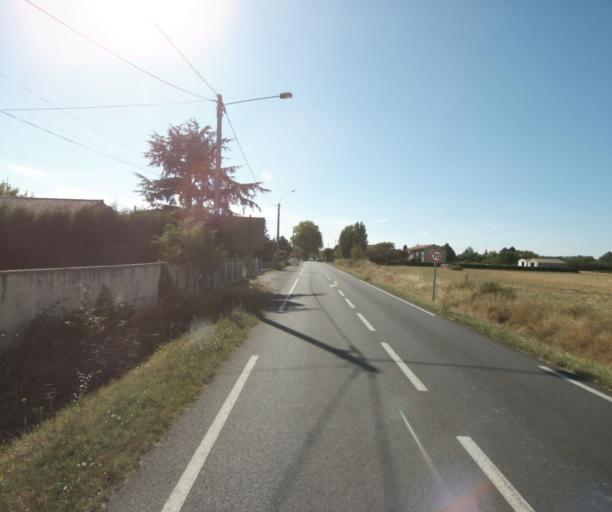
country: FR
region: Midi-Pyrenees
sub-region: Departement de la Haute-Garonne
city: Revel
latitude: 43.4652
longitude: 1.9872
